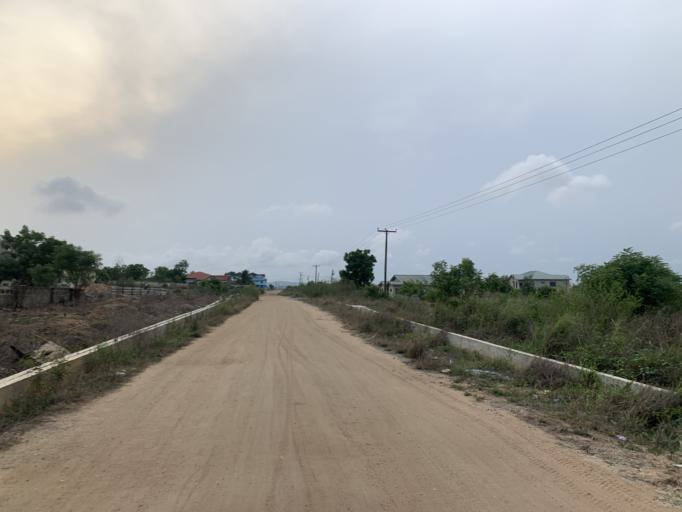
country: GH
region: Central
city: Winneba
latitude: 5.3818
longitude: -0.6235
